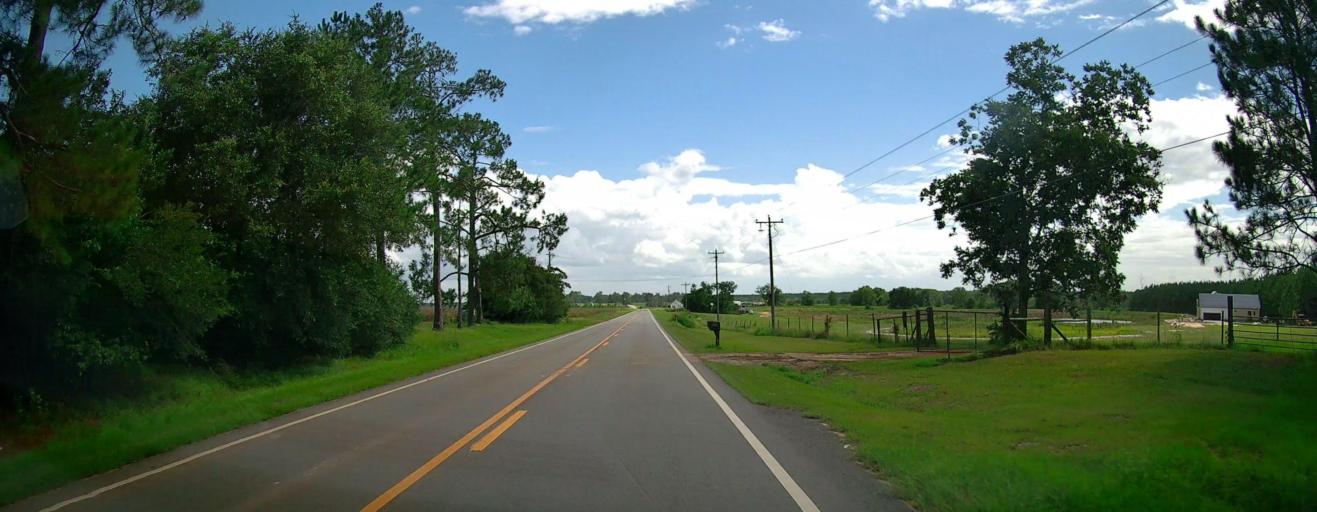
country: US
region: Georgia
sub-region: Irwin County
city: Ocilla
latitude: 31.6180
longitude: -83.1652
